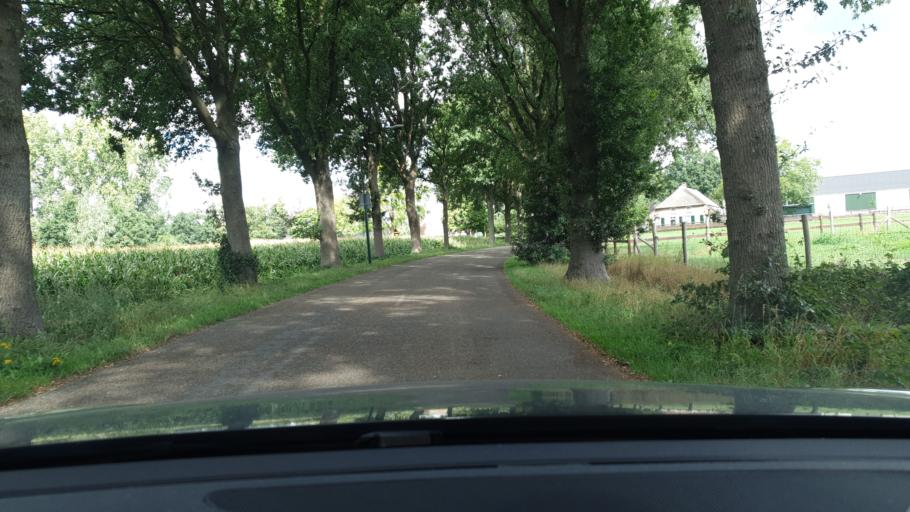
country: NL
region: North Brabant
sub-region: Gemeente Veghel
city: Zijtaart
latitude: 51.5976
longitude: 5.5395
